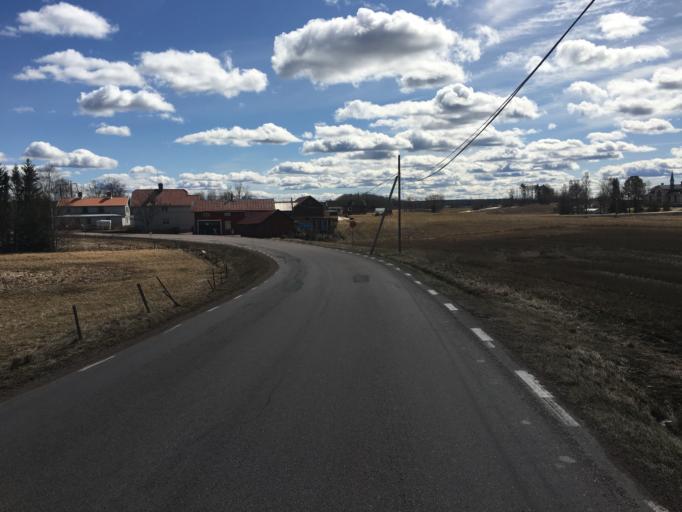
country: SE
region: Gaevleborg
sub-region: Hofors Kommun
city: Hofors
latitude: 60.5110
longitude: 16.4596
